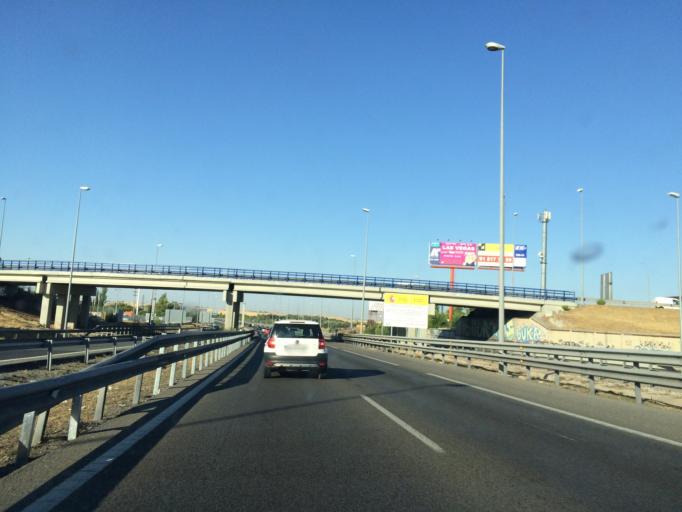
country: ES
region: Madrid
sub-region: Provincia de Madrid
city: Mostoles
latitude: 40.3343
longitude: -3.8848
